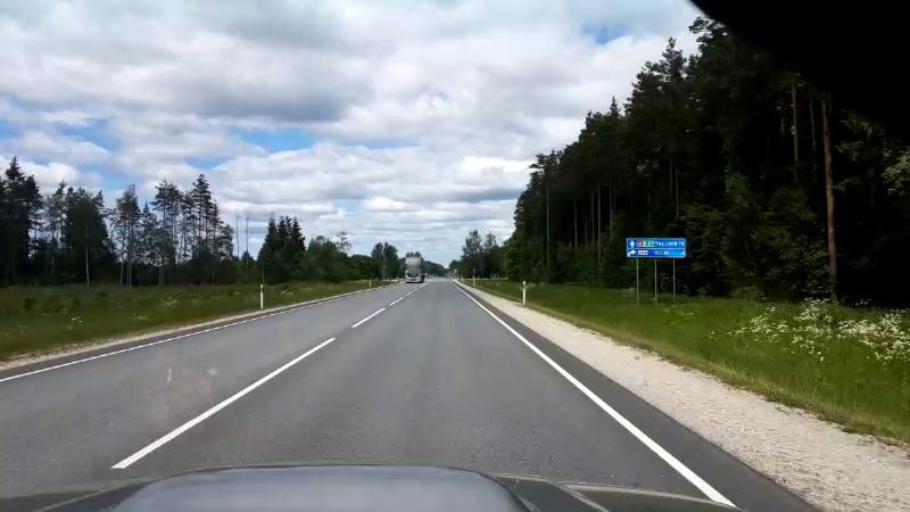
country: EE
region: Raplamaa
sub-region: Maerjamaa vald
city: Marjamaa
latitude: 58.8070
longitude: 24.4127
